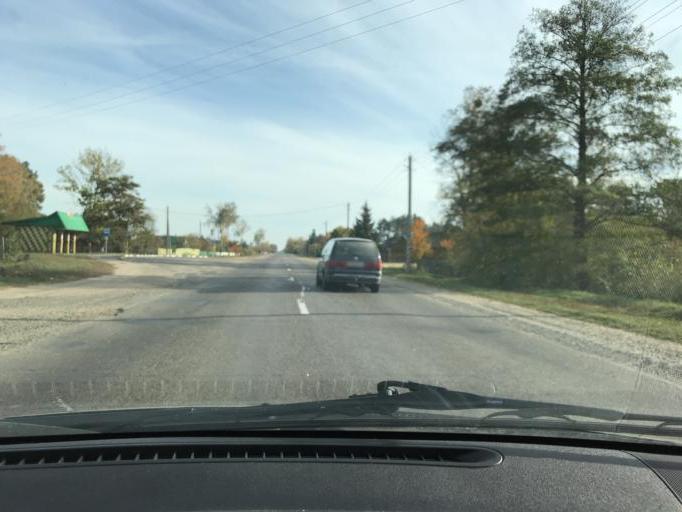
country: BY
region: Brest
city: Asnyezhytsy
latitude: 52.2244
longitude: 26.0273
